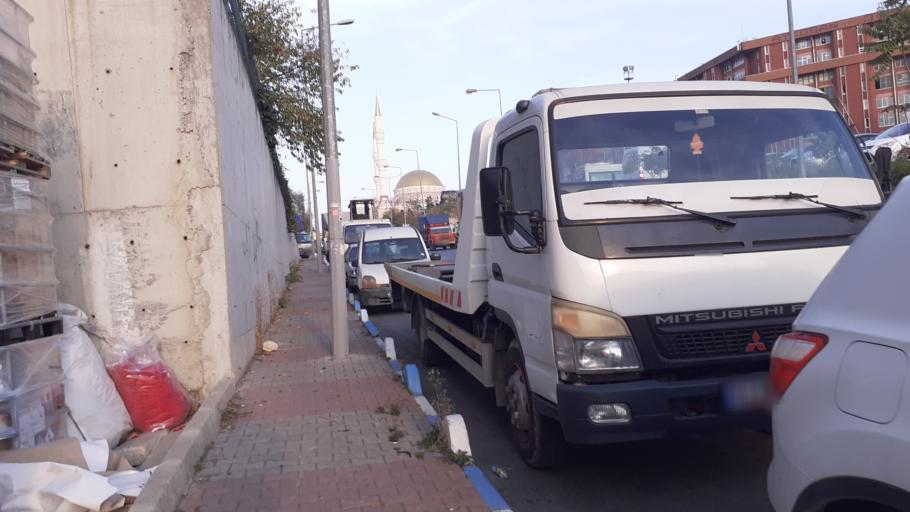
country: TR
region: Istanbul
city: Basaksehir
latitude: 41.0724
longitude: 28.7959
